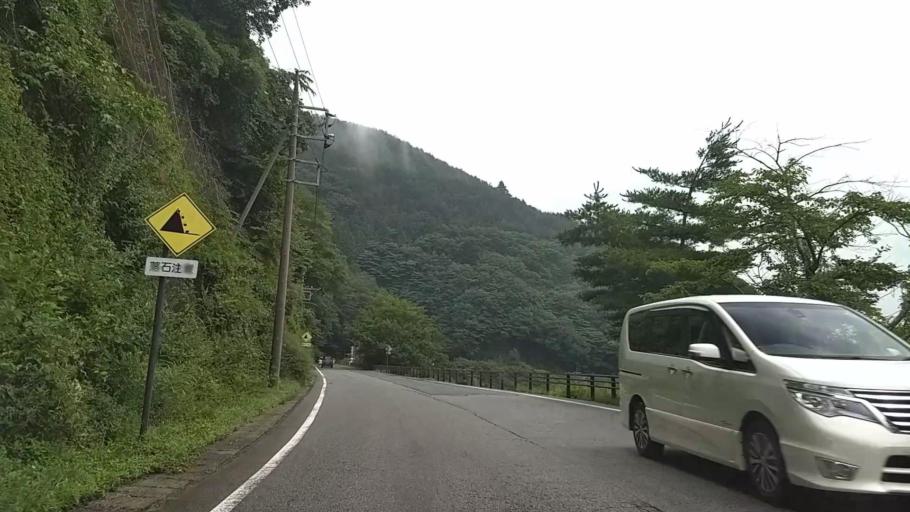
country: JP
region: Yamanashi
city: Fujikawaguchiko
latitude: 35.4888
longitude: 138.6121
